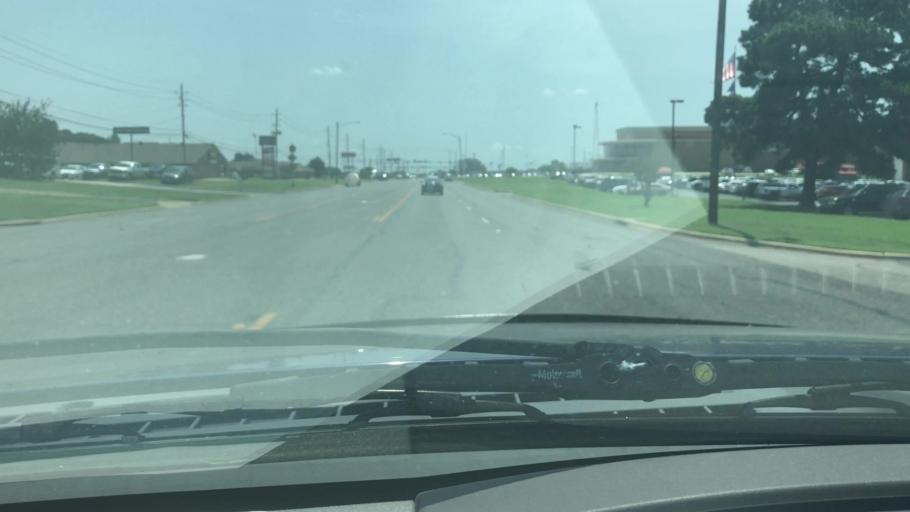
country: US
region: Arkansas
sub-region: Miller County
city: Texarkana
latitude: 33.4577
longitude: -94.0655
